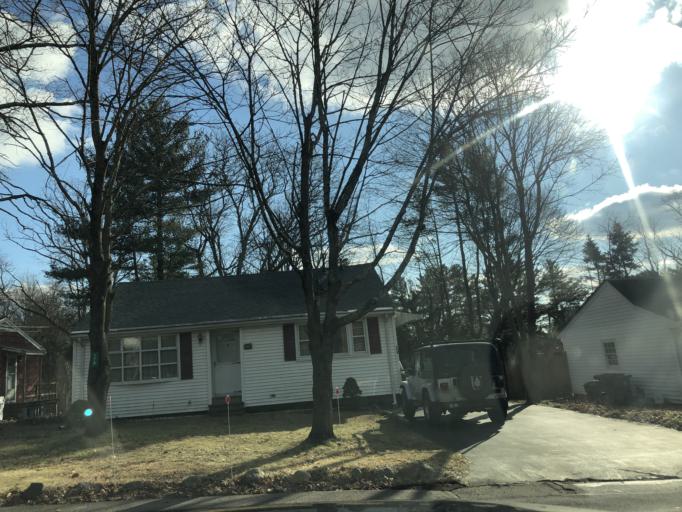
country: US
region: Massachusetts
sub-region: Plymouth County
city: Brockton
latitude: 42.1046
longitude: -71.0090
